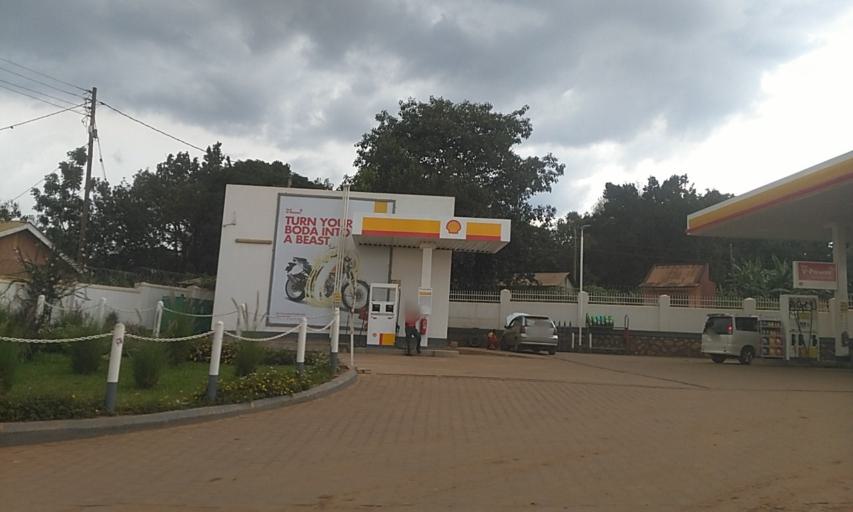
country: UG
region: Central Region
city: Kampala Central Division
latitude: 0.3180
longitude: 32.5110
